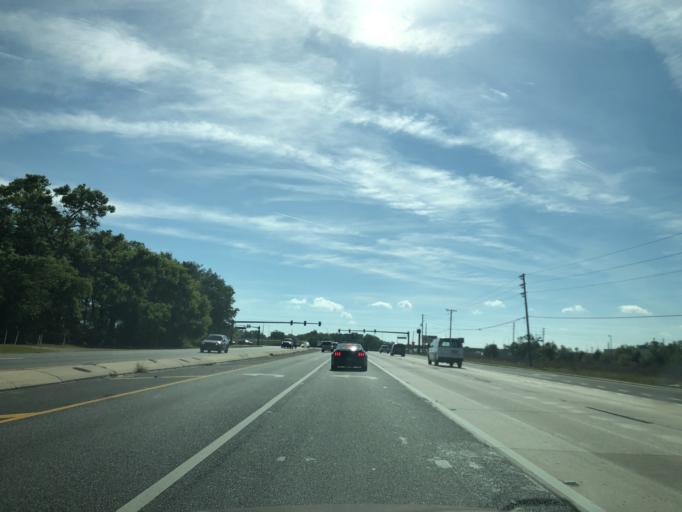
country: US
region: Florida
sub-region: Orange County
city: Zellwood
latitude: 28.6969
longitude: -81.5645
